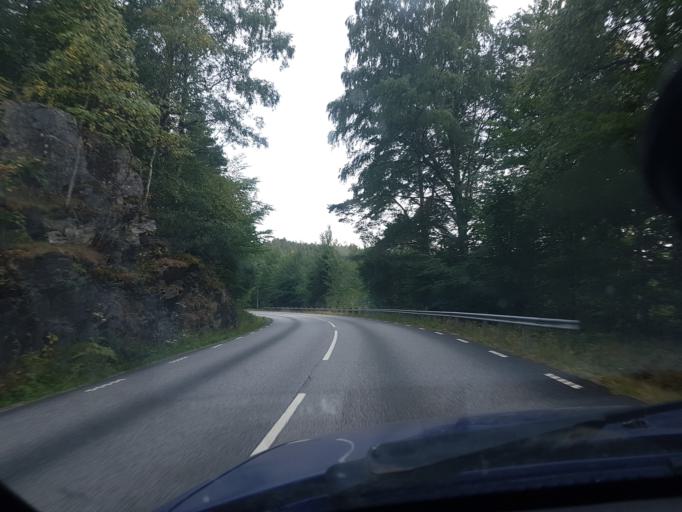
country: SE
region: Vaestra Goetaland
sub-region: Lysekils Kommun
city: Lysekil
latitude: 58.2767
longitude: 11.5317
